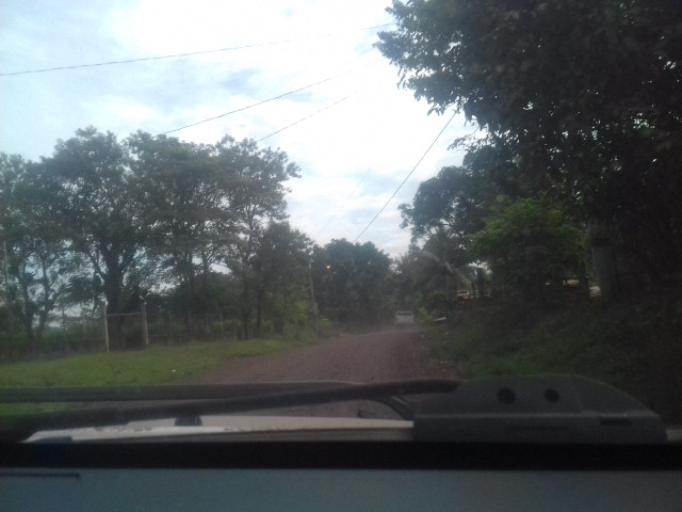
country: NI
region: Atlantico Norte (RAAN)
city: Waslala
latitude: 13.3982
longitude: -85.3236
